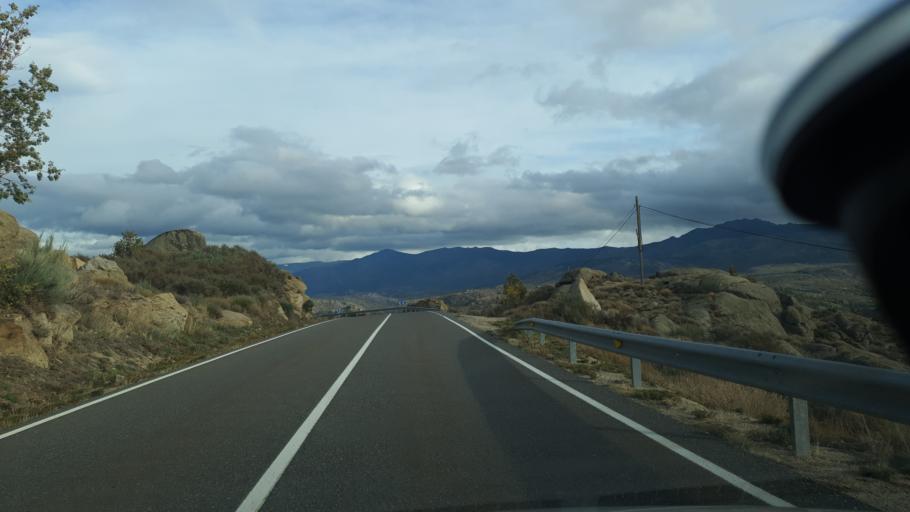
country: ES
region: Castille and Leon
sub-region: Provincia de Avila
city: Navalosa
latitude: 40.3940
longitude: -4.9145
